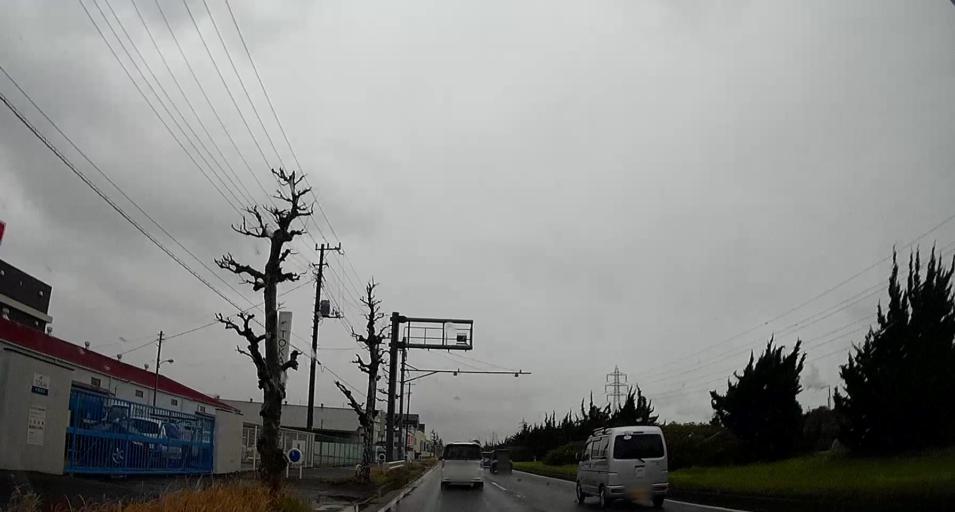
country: JP
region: Chiba
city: Ichihara
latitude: 35.5185
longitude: 140.0610
